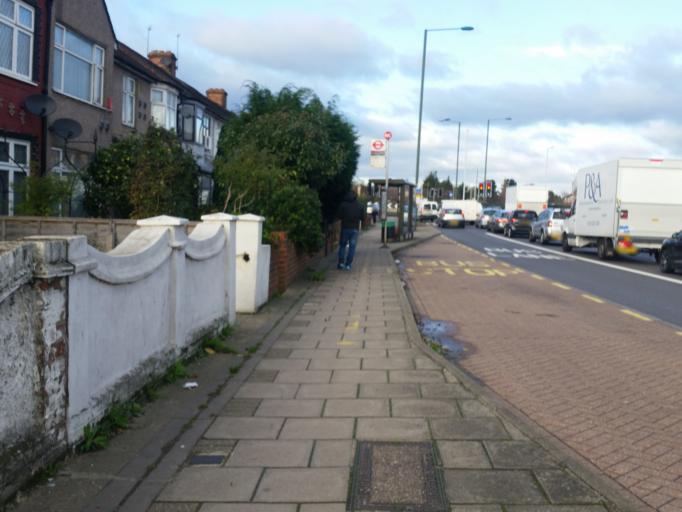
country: GB
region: England
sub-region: Greater London
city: Wood Green
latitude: 51.6151
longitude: -0.0870
